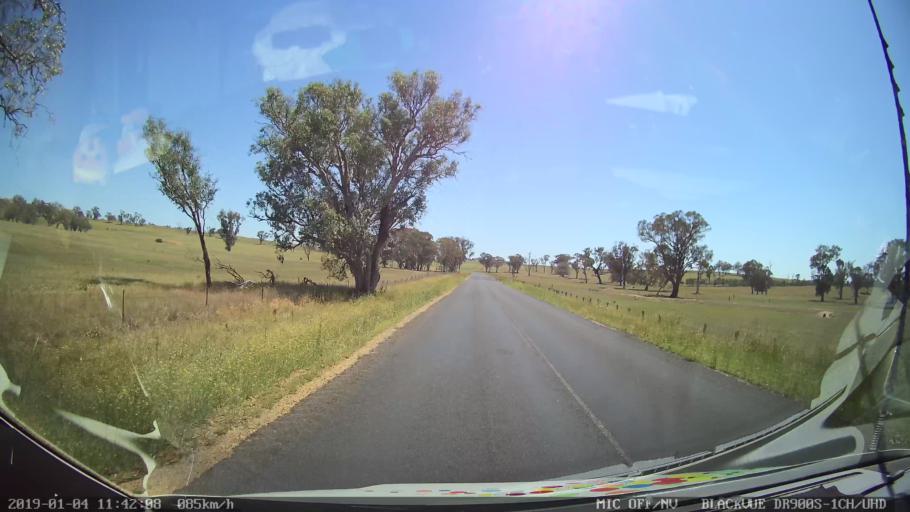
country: AU
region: New South Wales
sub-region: Cabonne
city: Molong
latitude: -32.9852
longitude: 148.7866
